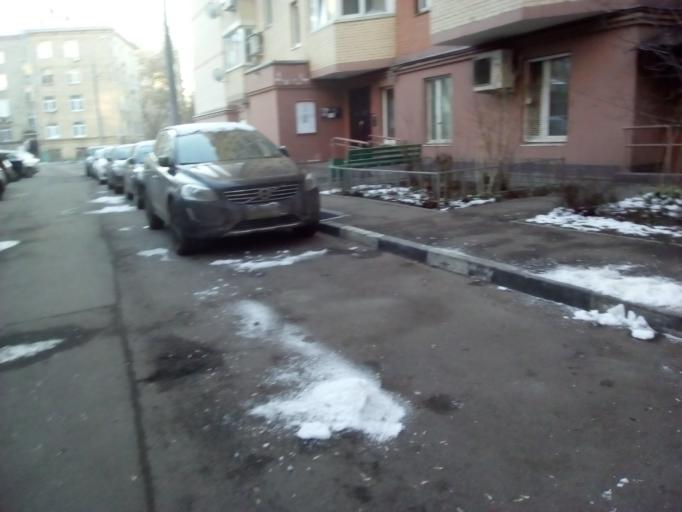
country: RU
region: Moskovskaya
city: Dorogomilovo
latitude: 55.7685
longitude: 37.5756
